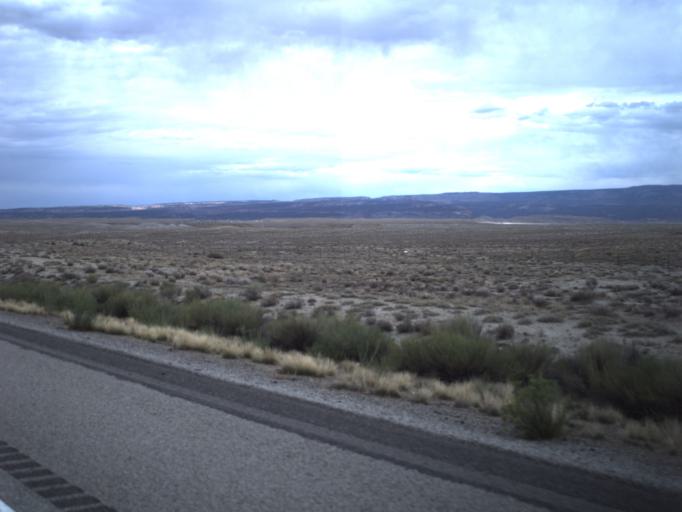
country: US
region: Utah
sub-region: Grand County
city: Moab
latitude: 38.9621
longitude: -109.3765
